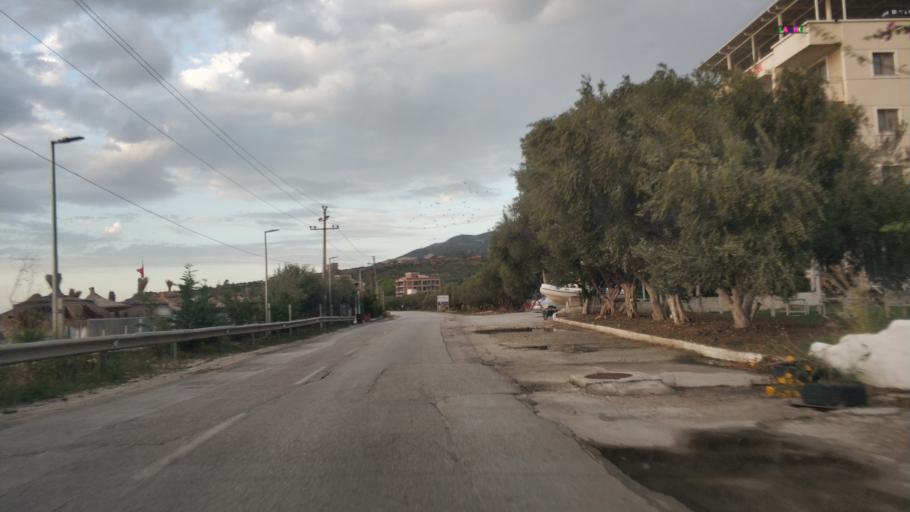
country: AL
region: Vlore
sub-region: Rrethi i Vlores
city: Orikum
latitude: 40.3497
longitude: 19.4854
